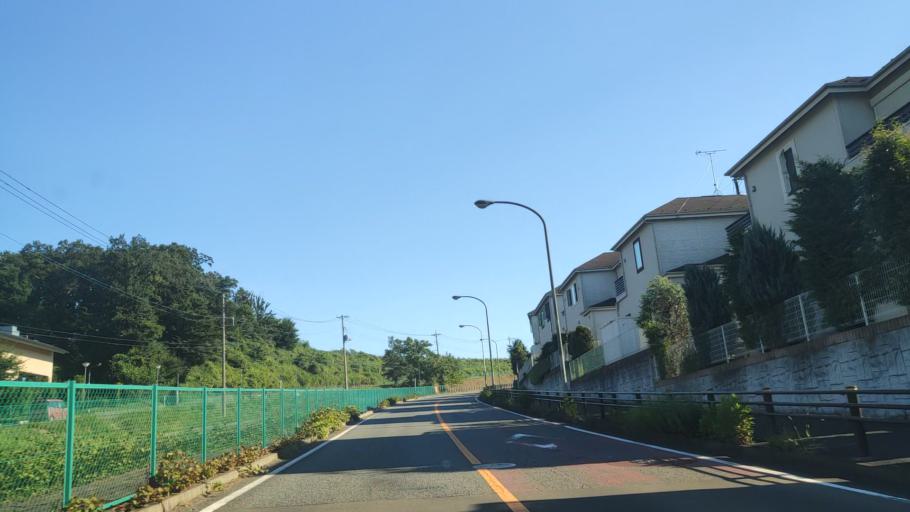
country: JP
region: Tokyo
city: Hachioji
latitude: 35.6410
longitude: 139.3318
